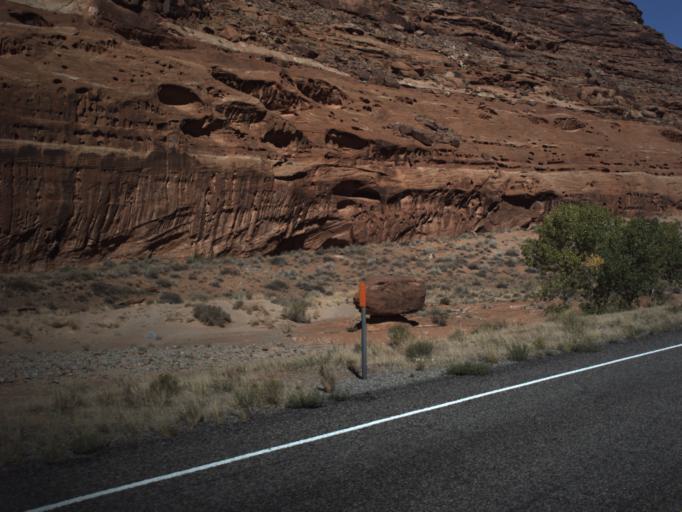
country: US
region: Utah
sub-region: San Juan County
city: Blanding
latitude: 37.9790
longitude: -110.4925
